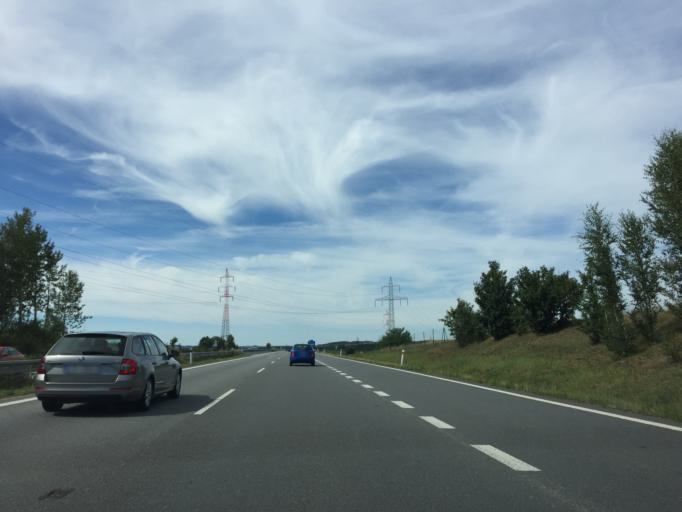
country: CZ
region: Jihocesky
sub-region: Okres Tabor
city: Sezimovo Usti
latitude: 49.4249
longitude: 14.7016
